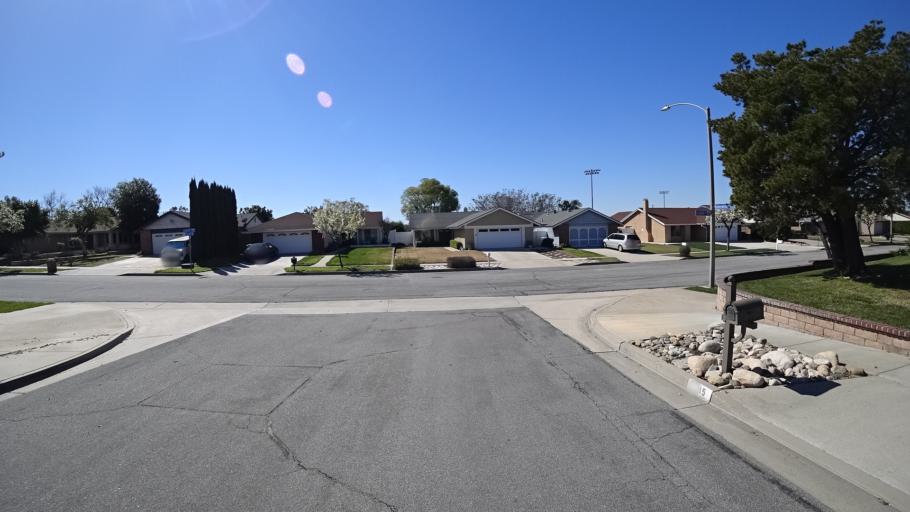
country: US
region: California
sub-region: Orange County
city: Yorba Linda
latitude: 33.8688
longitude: -117.7974
